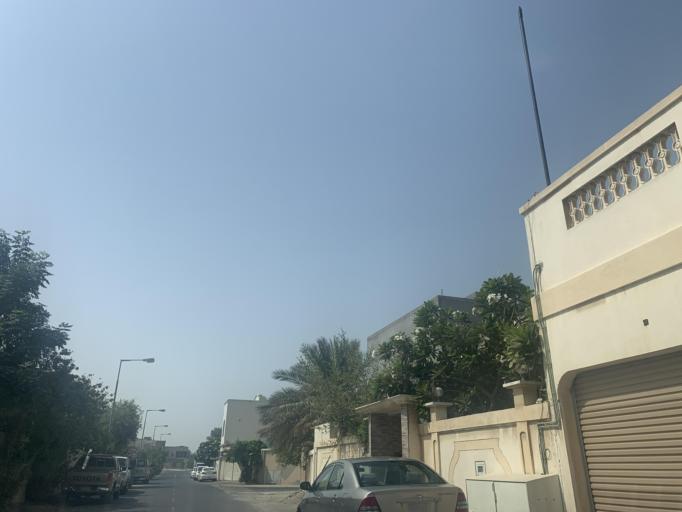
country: BH
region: Manama
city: Jidd Hafs
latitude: 26.2074
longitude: 50.4617
